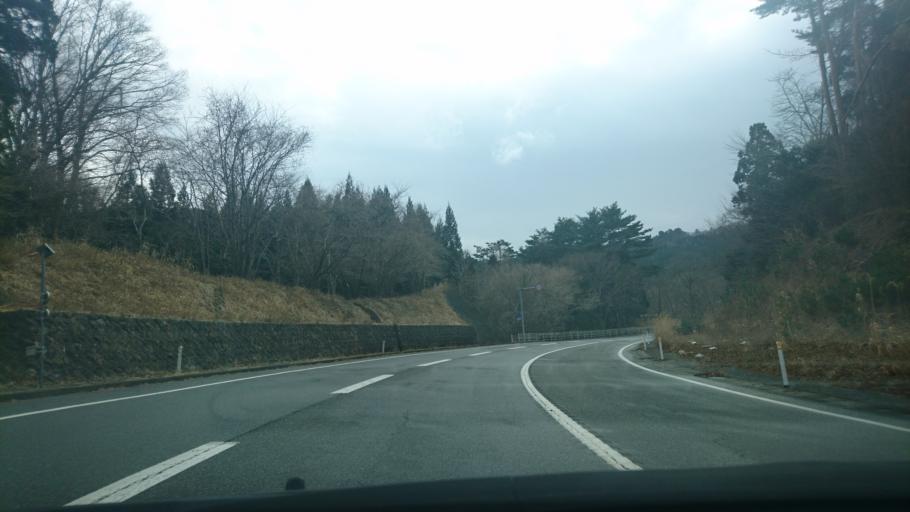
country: JP
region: Iwate
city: Ofunato
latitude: 39.1397
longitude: 141.8266
